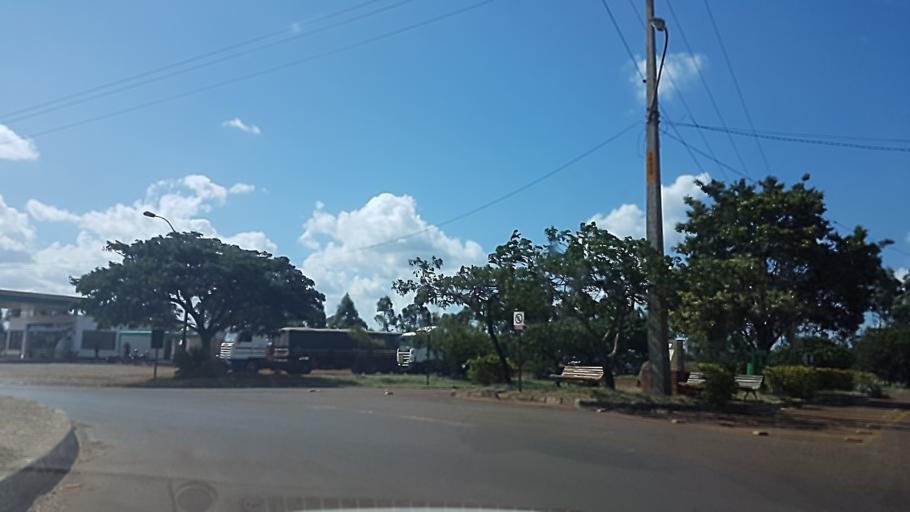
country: PY
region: Itapua
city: Carmen del Parana
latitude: -27.2198
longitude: -56.1380
